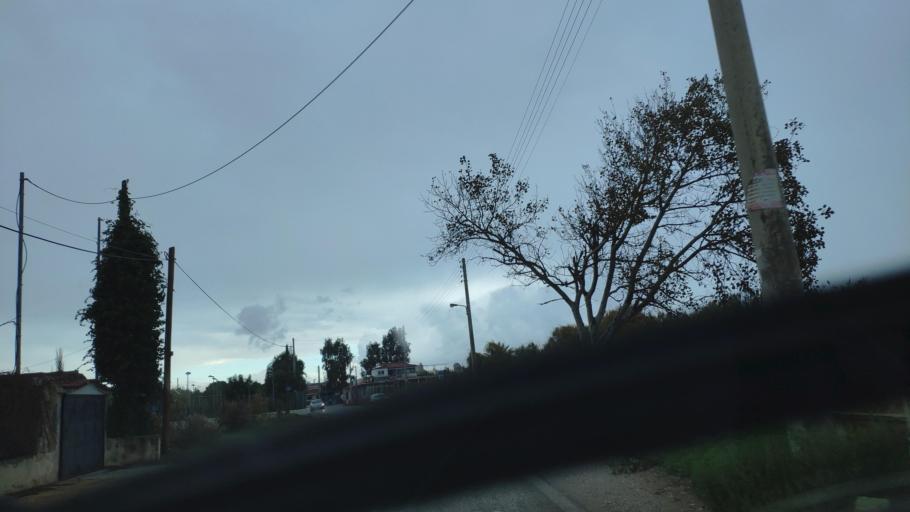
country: GR
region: Attica
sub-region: Nomarchia Anatolikis Attikis
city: Artemida
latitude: 37.9885
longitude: 24.0142
